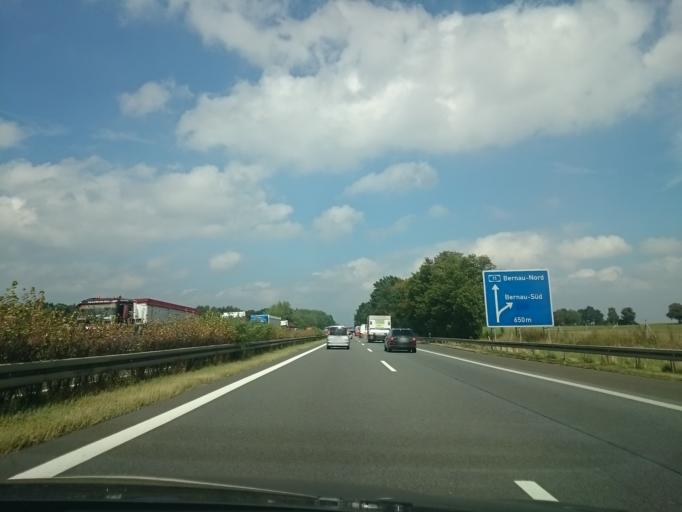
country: DE
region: Brandenburg
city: Bernau bei Berlin
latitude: 52.6420
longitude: 13.5670
